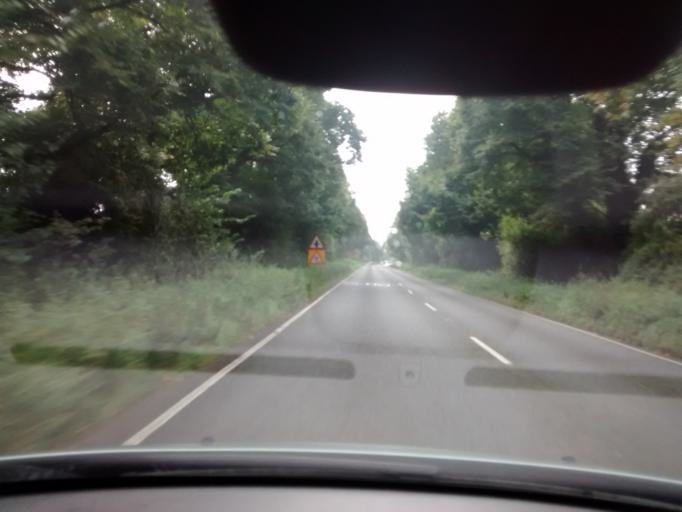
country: GB
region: England
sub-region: Hampshire
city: Ringwood
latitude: 50.8756
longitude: -1.7923
